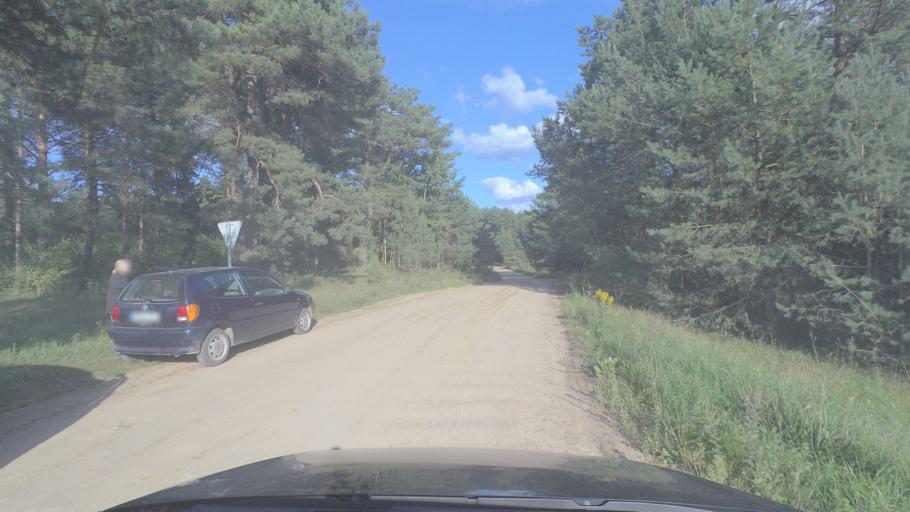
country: LT
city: Pabrade
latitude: 55.1397
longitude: 25.7119
